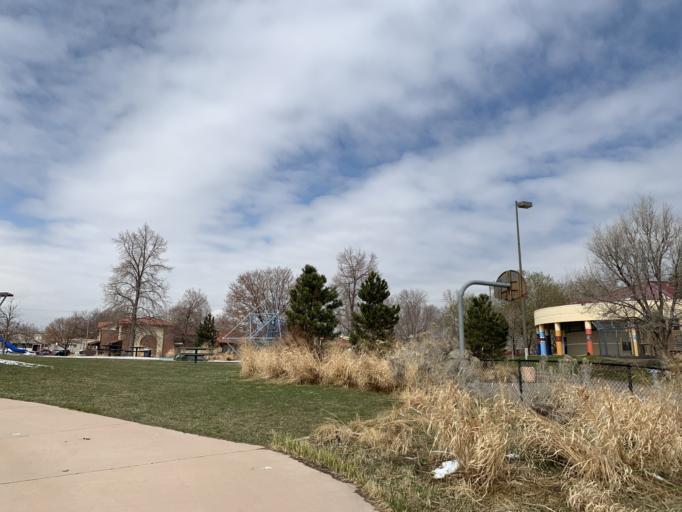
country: US
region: Colorado
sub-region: Denver County
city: Denver
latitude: 39.7322
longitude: -105.0174
